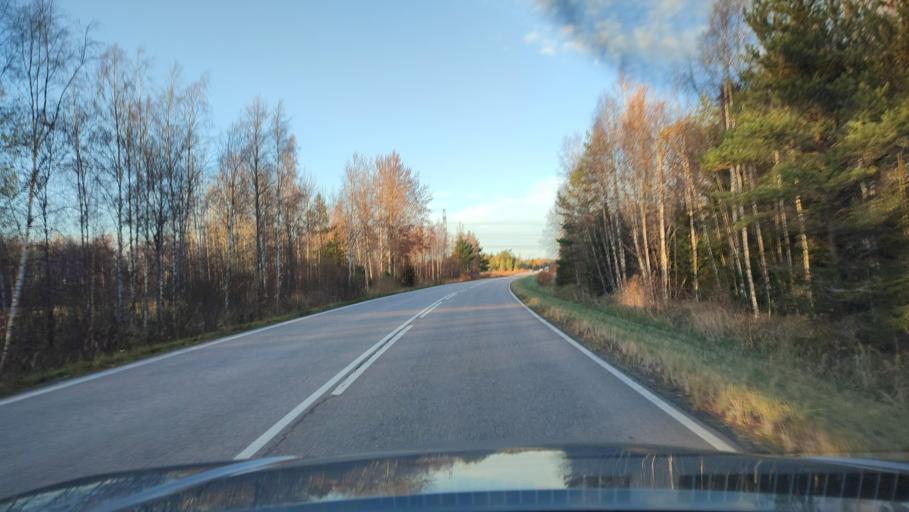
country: FI
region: Ostrobothnia
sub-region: Sydosterbotten
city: Kristinestad
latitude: 62.2891
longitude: 21.3778
